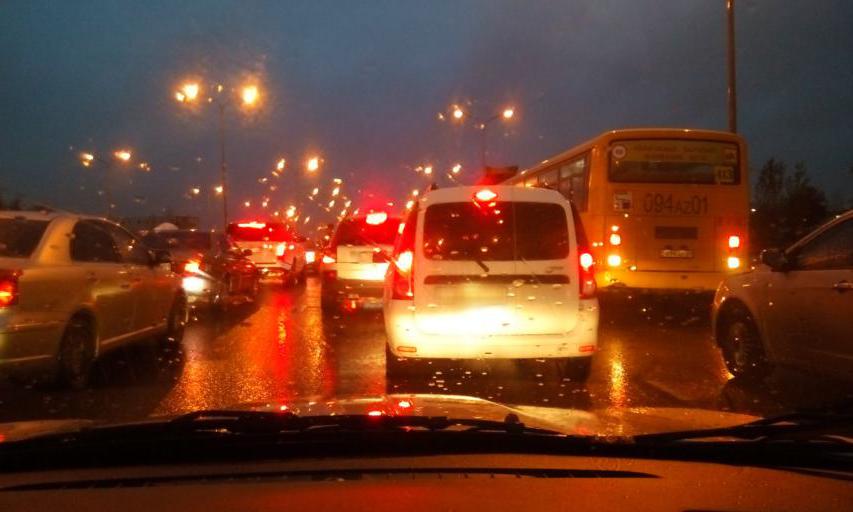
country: KZ
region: Astana Qalasy
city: Astana
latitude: 51.1807
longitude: 71.3767
